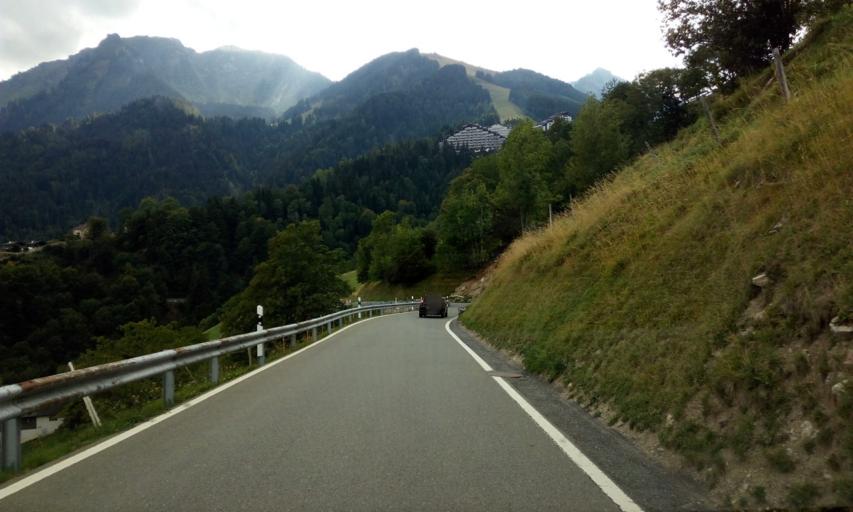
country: CH
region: Valais
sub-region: Monthey District
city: Vouvry
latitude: 46.3195
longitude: 6.8794
